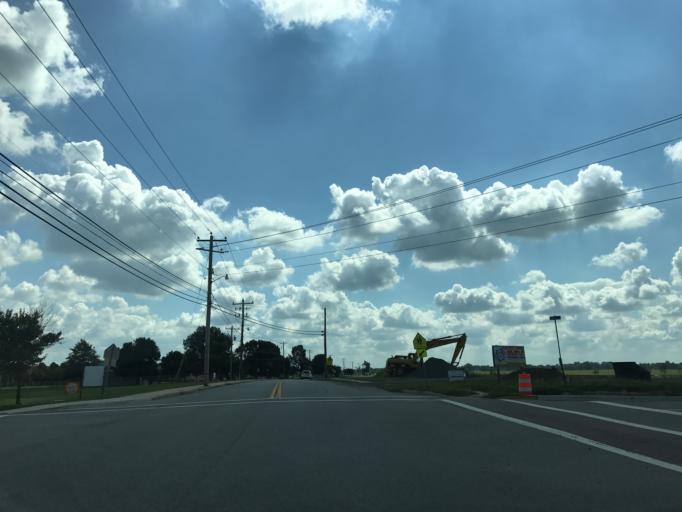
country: US
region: Maryland
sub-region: Queen Anne's County
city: Centreville
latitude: 39.0390
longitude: -76.0568
